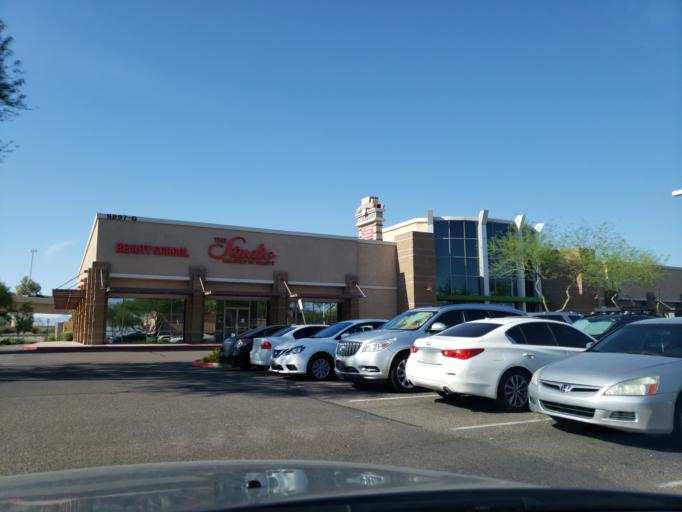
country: US
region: Arizona
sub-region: Maricopa County
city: Tolleson
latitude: 33.4638
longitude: -112.2701
